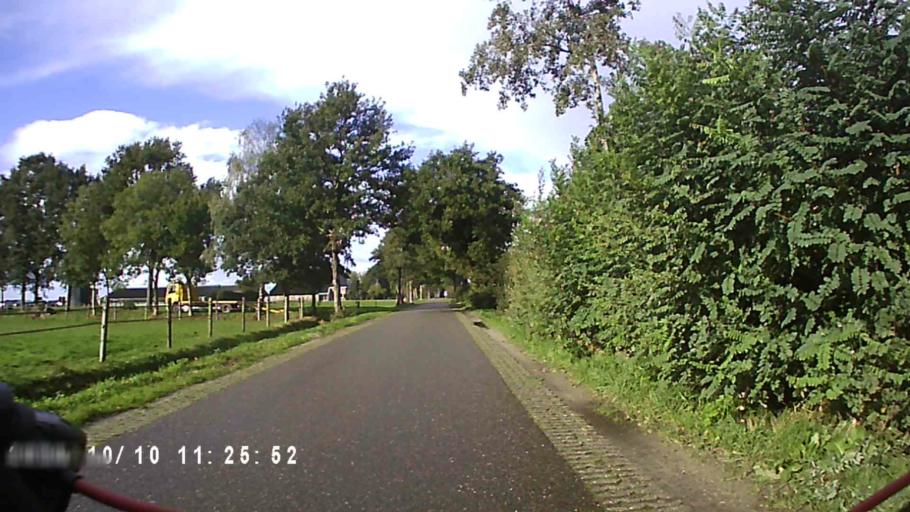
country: NL
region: Friesland
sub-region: Gemeente Smallingerland
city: Drachtstercompagnie
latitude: 53.0877
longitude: 6.1670
